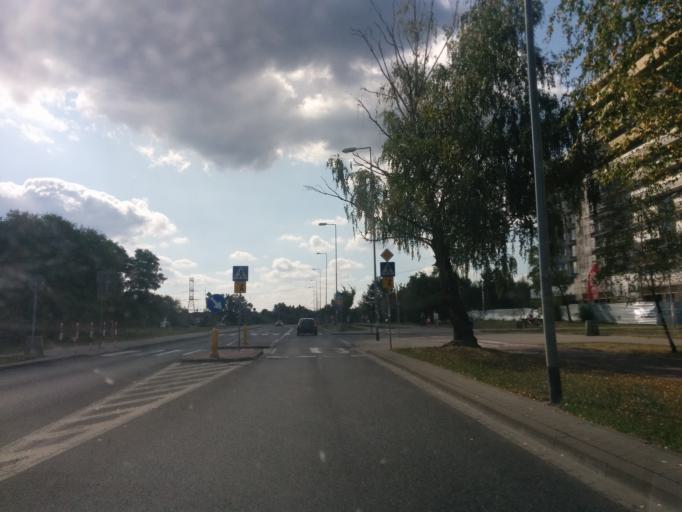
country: PL
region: Masovian Voivodeship
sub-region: Warszawa
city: Bialoleka
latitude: 52.3295
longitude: 20.9410
